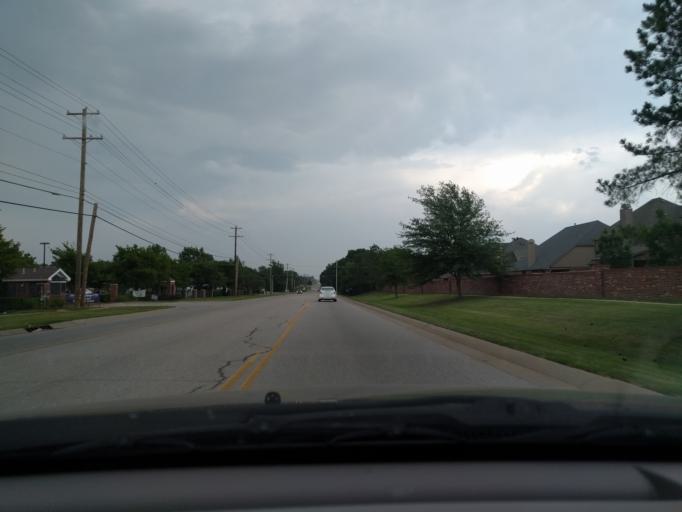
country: US
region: Oklahoma
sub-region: Tulsa County
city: Broken Arrow
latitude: 36.0463
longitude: -95.8442
